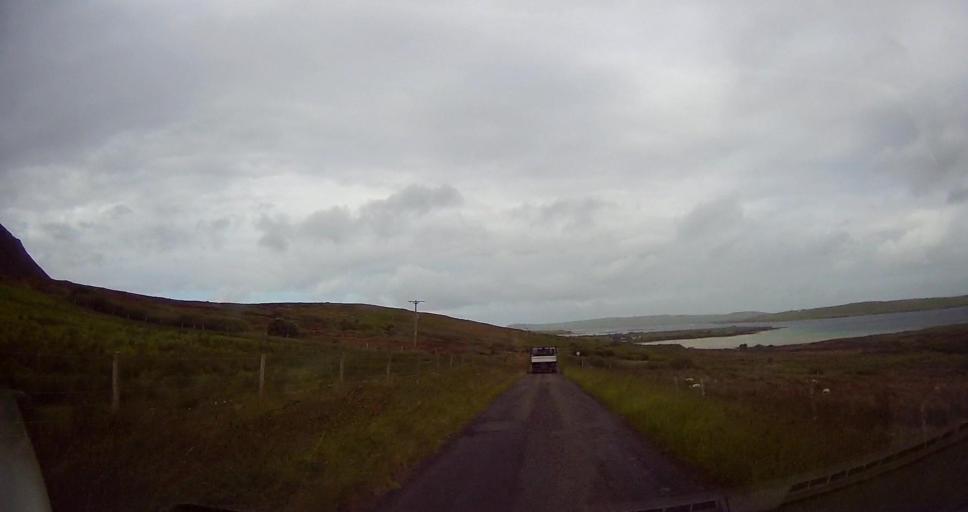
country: GB
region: Scotland
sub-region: Orkney Islands
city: Stromness
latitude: 58.9011
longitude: -3.3153
